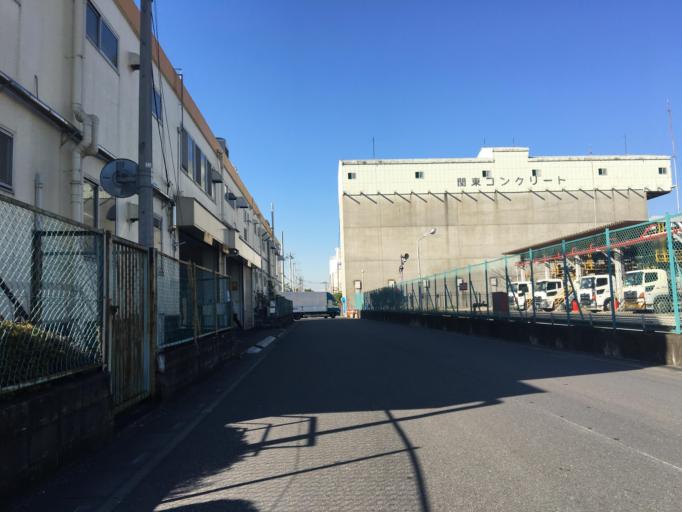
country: JP
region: Saitama
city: Yashio-shi
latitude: 35.7999
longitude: 139.8491
